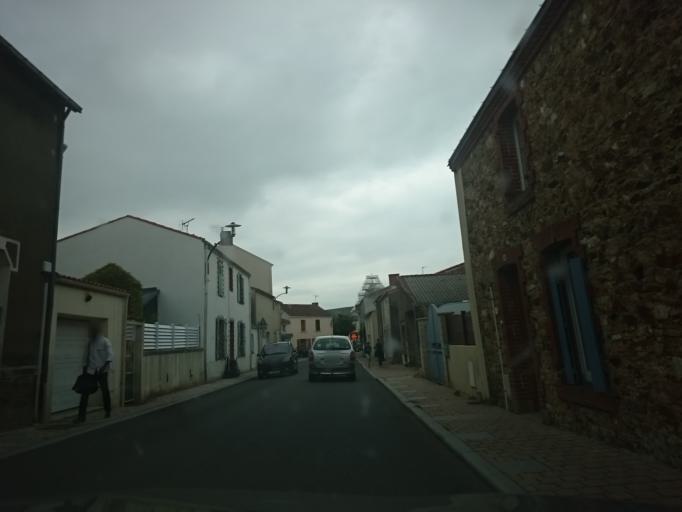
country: FR
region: Pays de la Loire
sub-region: Departement de la Loire-Atlantique
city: Saint-Jean-de-Boiseau
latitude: 47.1949
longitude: -1.7228
